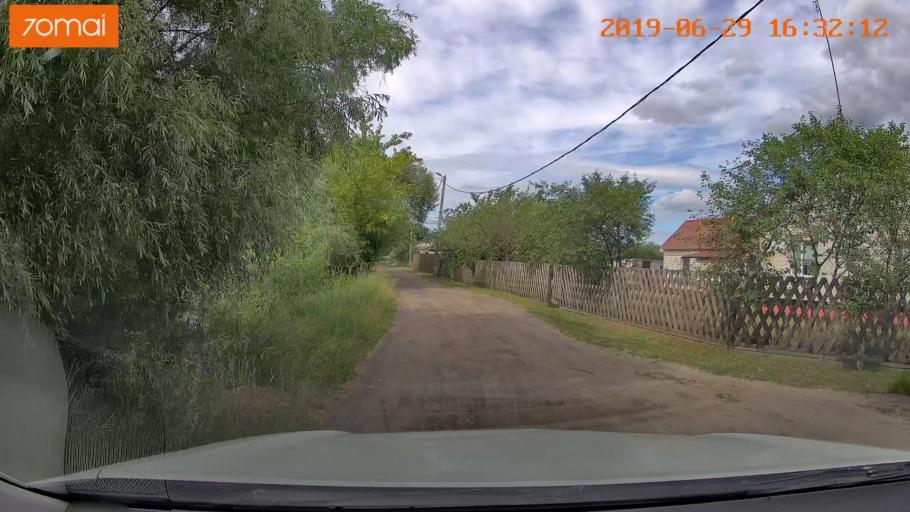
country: BY
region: Brest
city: Luninyets
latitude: 52.2009
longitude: 27.0107
